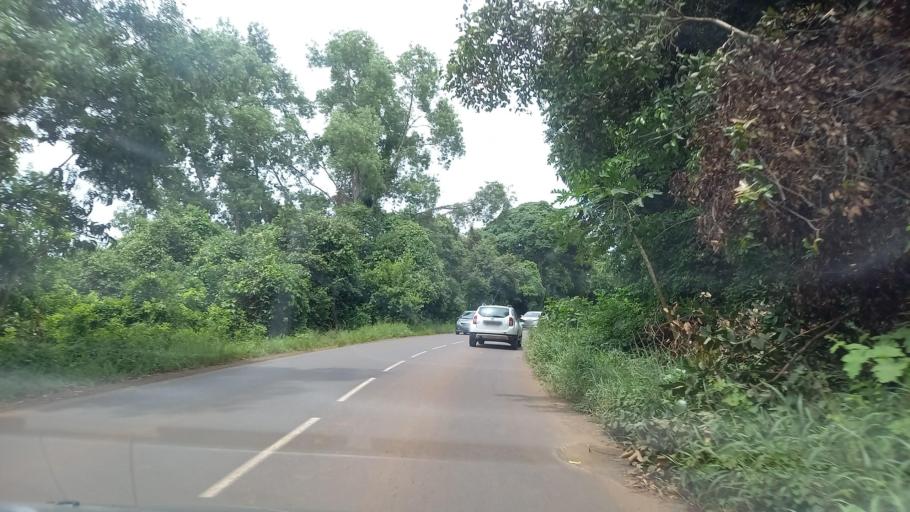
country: YT
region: Tsingoni
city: Tsingoni
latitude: -12.7989
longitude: 45.1288
